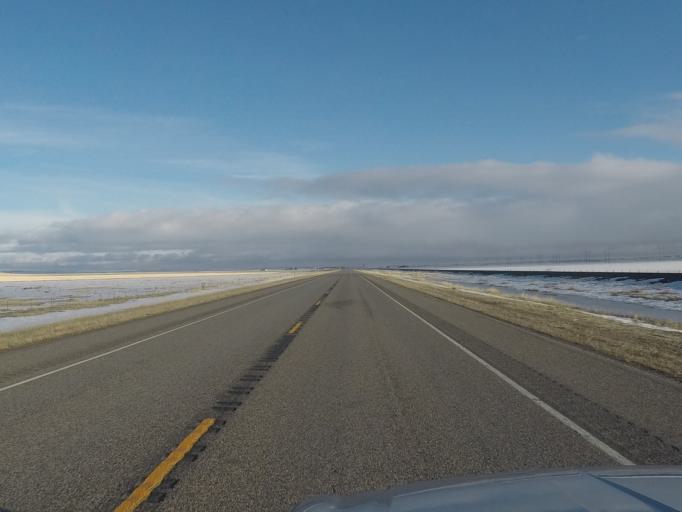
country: US
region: Montana
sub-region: Yellowstone County
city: Laurel
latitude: 46.0152
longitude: -108.7962
